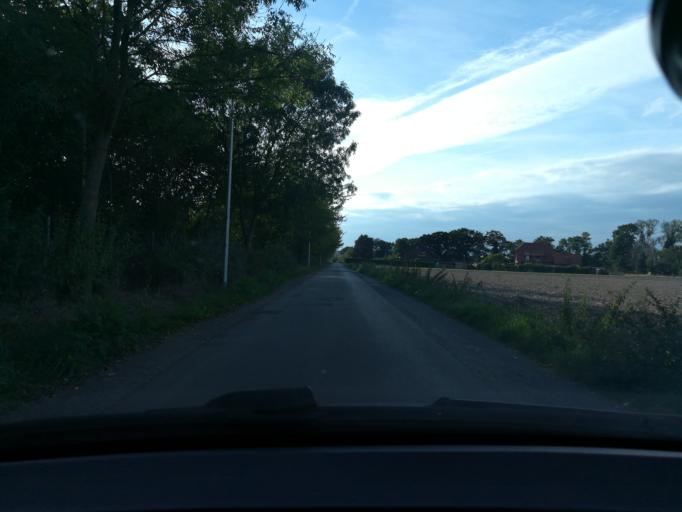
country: DE
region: North Rhine-Westphalia
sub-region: Regierungsbezirk Detmold
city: Minden
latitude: 52.3102
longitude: 8.9592
